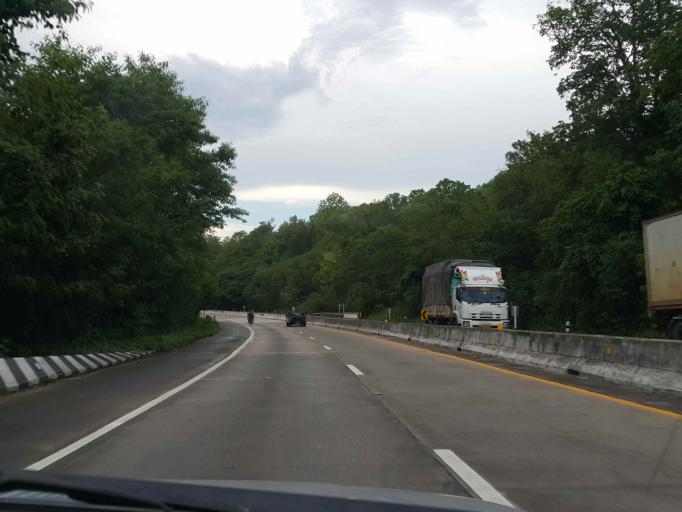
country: TH
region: Lampang
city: Hang Chat
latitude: 18.3407
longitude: 99.2469
